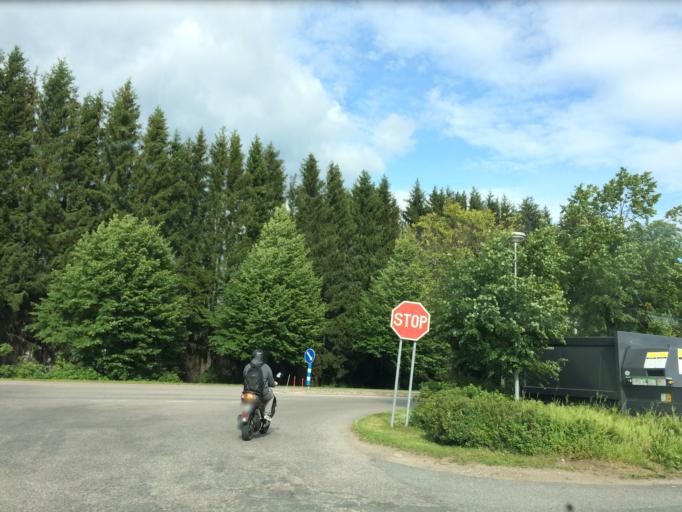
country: FI
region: Haeme
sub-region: Haemeenlinna
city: Turenki
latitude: 60.9220
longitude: 24.6500
